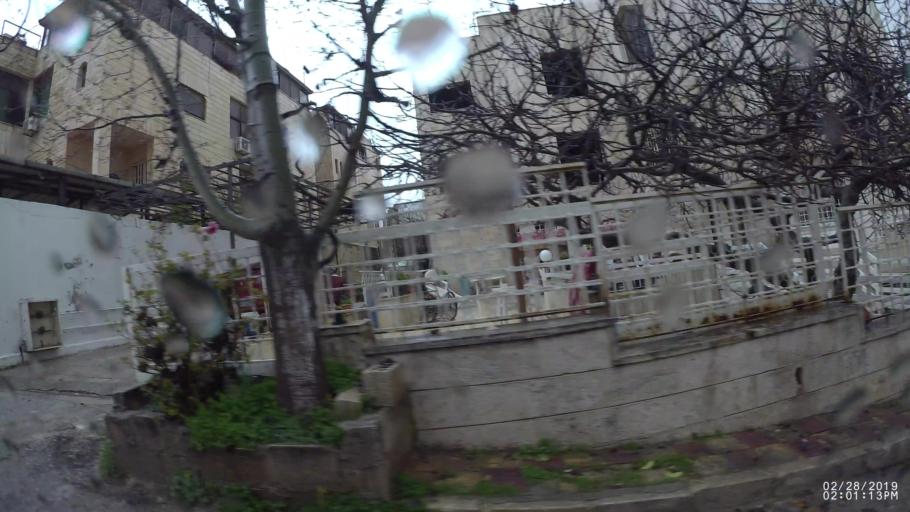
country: JO
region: Amman
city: Al Jubayhah
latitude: 32.0292
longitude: 35.8776
